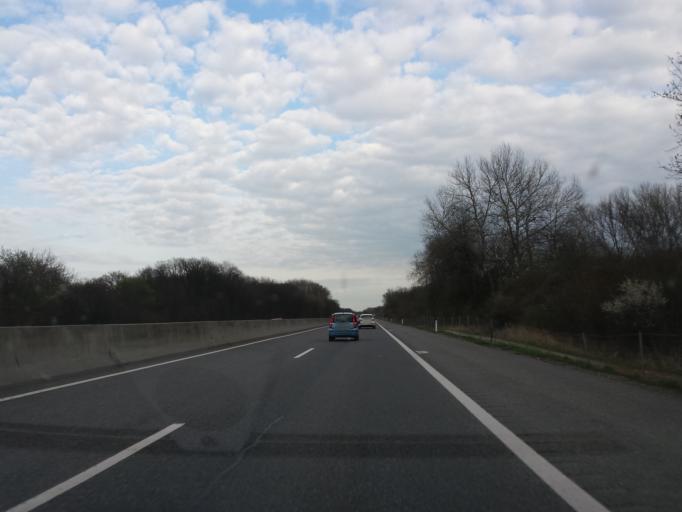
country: AT
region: Lower Austria
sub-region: Politischer Bezirk Korneuburg
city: Stetteldorf am Wagram
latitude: 48.3619
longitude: 15.9772
